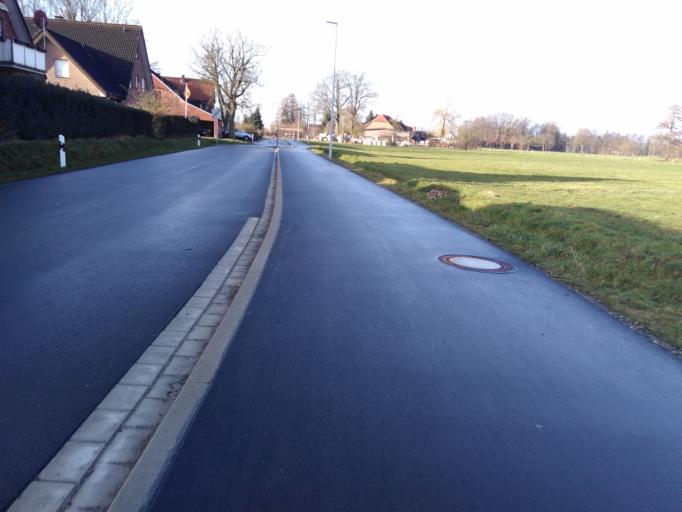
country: DE
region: North Rhine-Westphalia
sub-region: Regierungsbezirk Detmold
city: Verl
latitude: 51.8832
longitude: 8.4885
